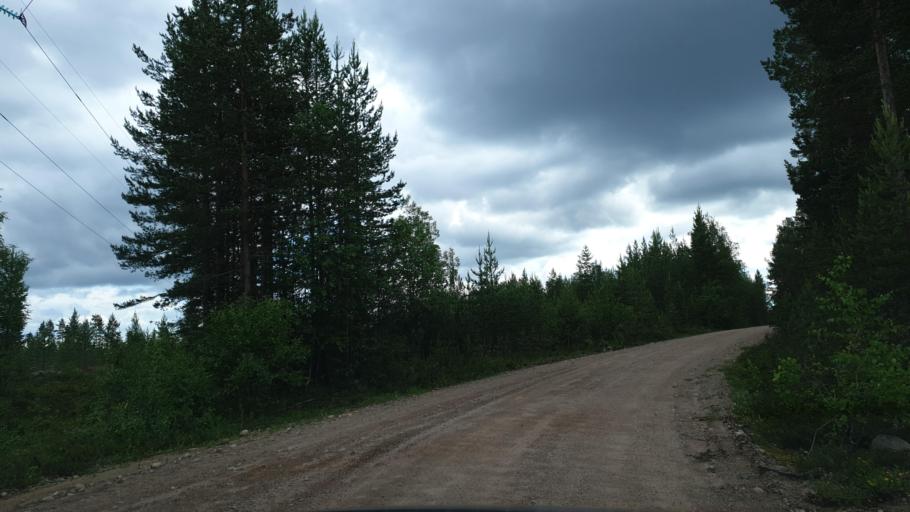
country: SE
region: Jaemtland
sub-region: Harjedalens Kommun
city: Sveg
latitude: 62.0404
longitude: 14.4979
